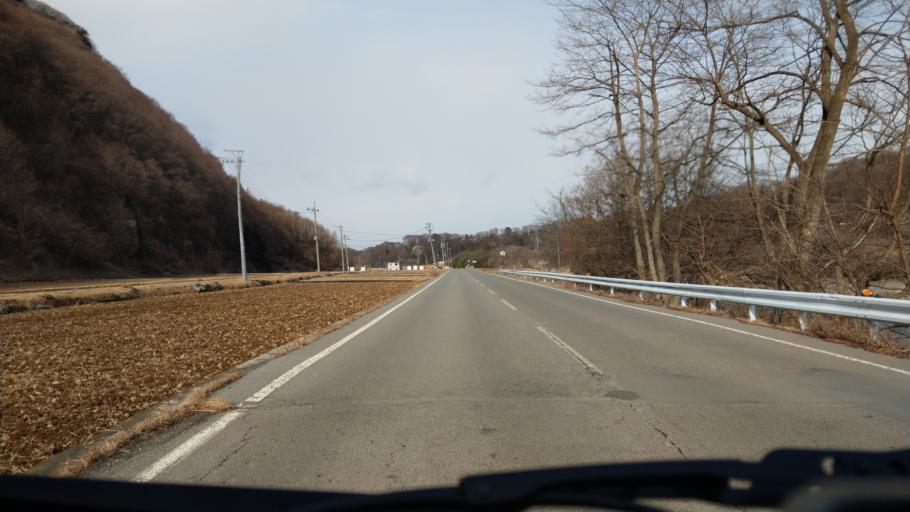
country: JP
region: Nagano
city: Komoro
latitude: 36.3346
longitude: 138.3846
